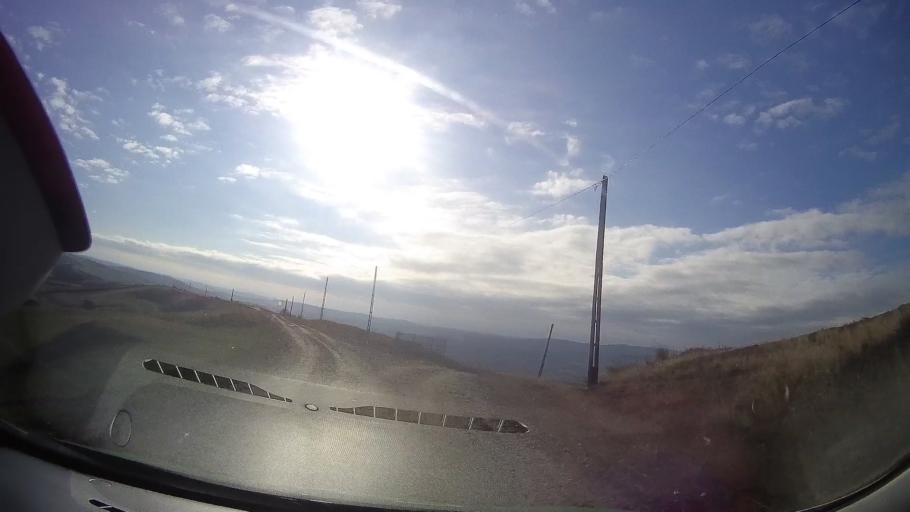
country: RO
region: Mures
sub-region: Comuna Saulia
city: Saulia
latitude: 46.5928
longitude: 24.2195
